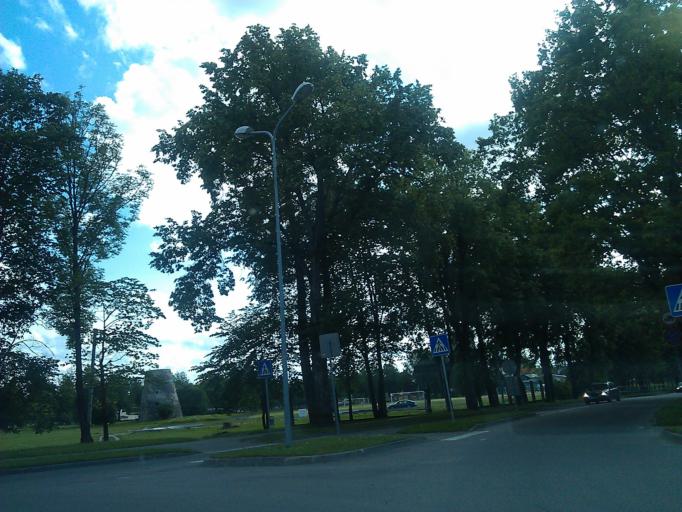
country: LV
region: Cesu Rajons
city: Cesis
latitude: 57.3174
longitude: 25.2824
